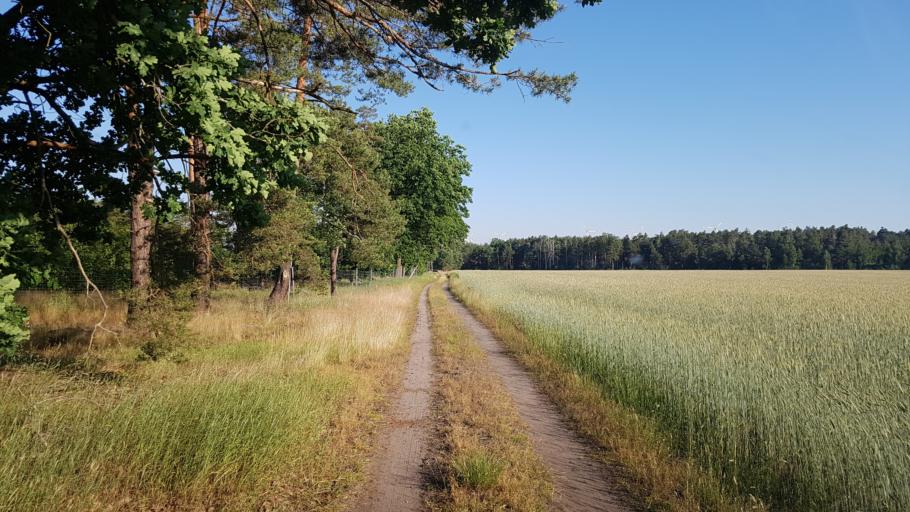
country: DE
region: Brandenburg
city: Schilda
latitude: 51.6366
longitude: 13.4026
